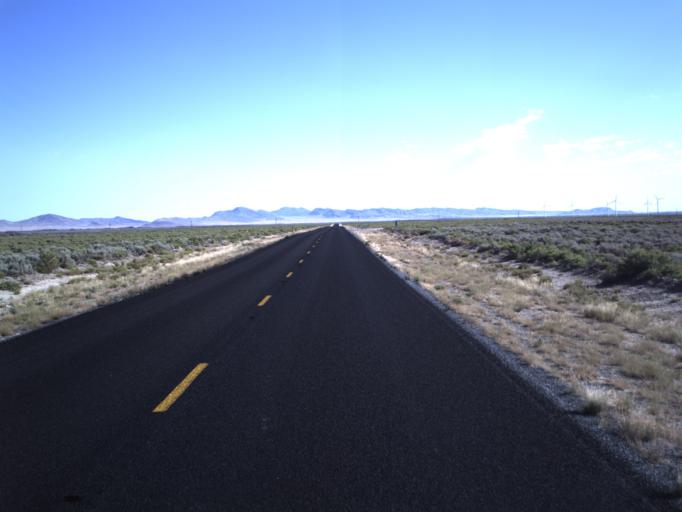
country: US
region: Utah
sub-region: Beaver County
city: Milford
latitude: 38.5379
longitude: -112.9912
